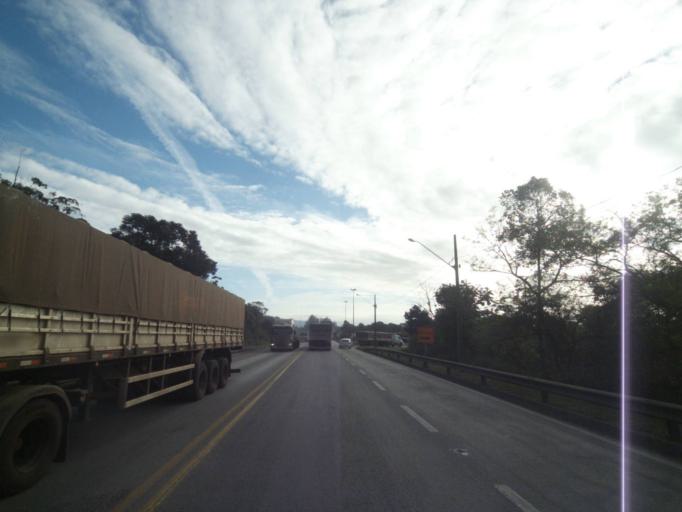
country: BR
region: Parana
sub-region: Paranagua
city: Paranagua
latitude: -25.5473
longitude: -48.5605
